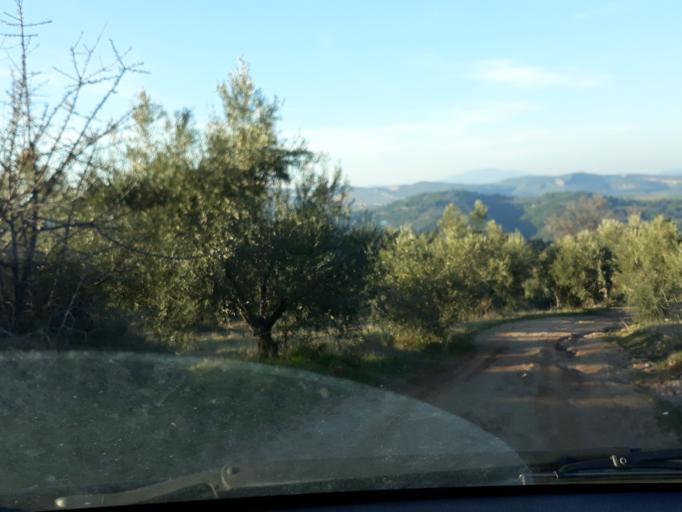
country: GR
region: Central Greece
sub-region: Nomos Voiotias
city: Asopia
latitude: 38.2713
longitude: 23.5324
